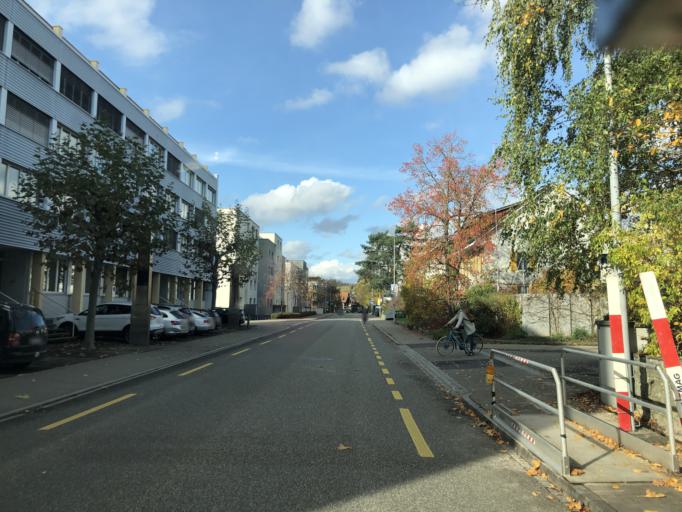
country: CH
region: Aargau
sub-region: Bezirk Baden
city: Wettingen
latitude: 47.4619
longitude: 8.3147
